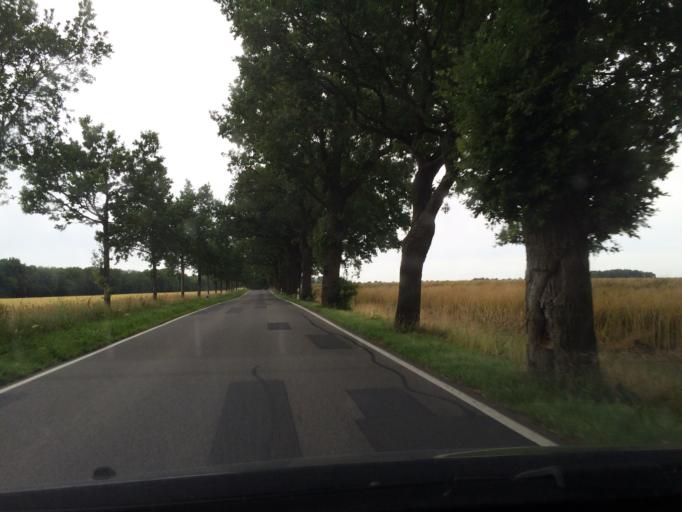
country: DE
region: Mecklenburg-Vorpommern
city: Prohn
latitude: 54.3894
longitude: 13.0037
